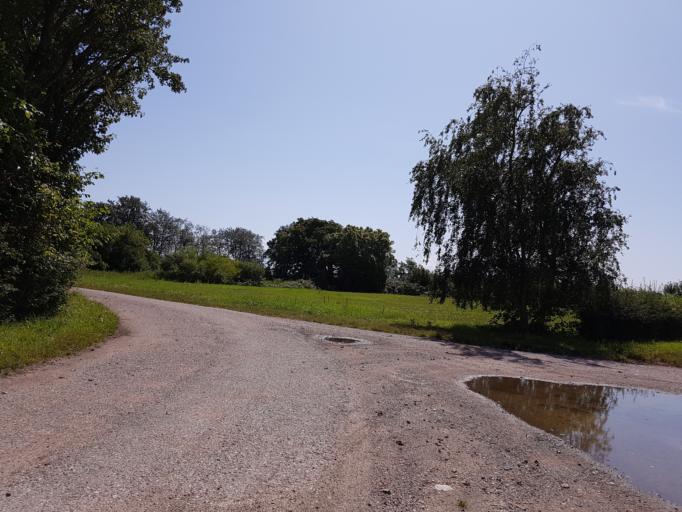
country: DK
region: Zealand
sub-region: Guldborgsund Kommune
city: Nykobing Falster
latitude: 54.5690
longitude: 11.9525
